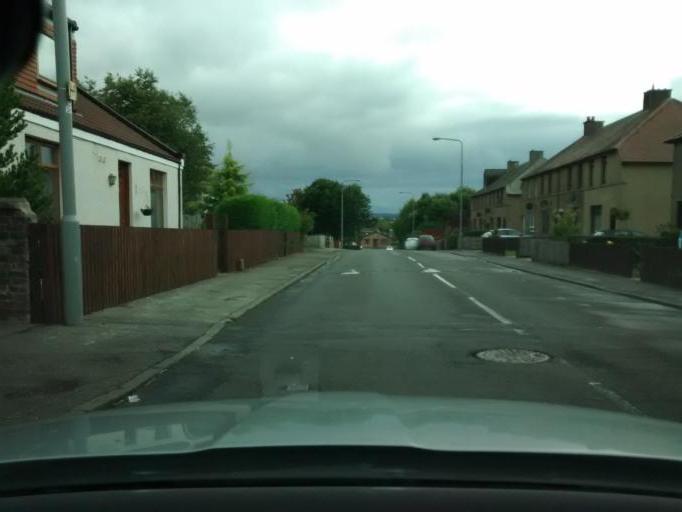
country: GB
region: Scotland
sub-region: West Lothian
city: Bathgate
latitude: 55.9026
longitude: -3.6575
